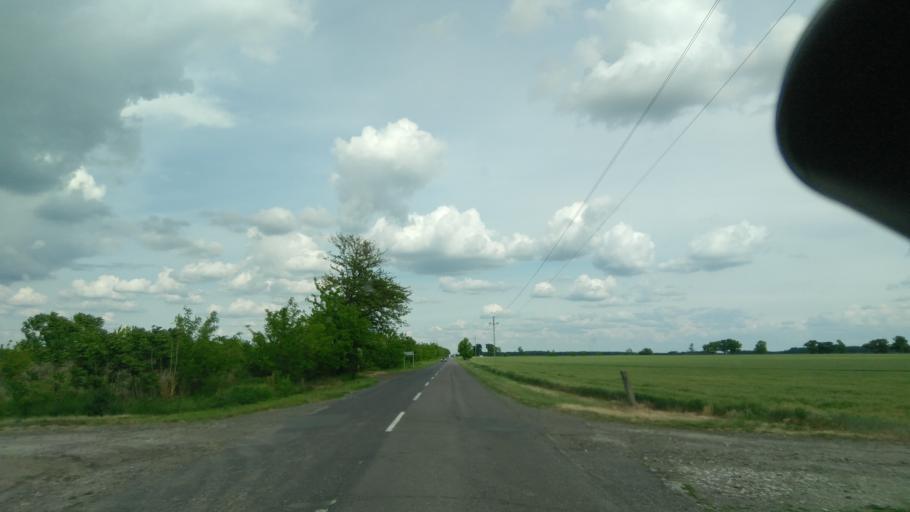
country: RO
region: Arad
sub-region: Comuna Peregu Mare
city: Peregu Mare
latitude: 46.3060
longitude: 20.8957
